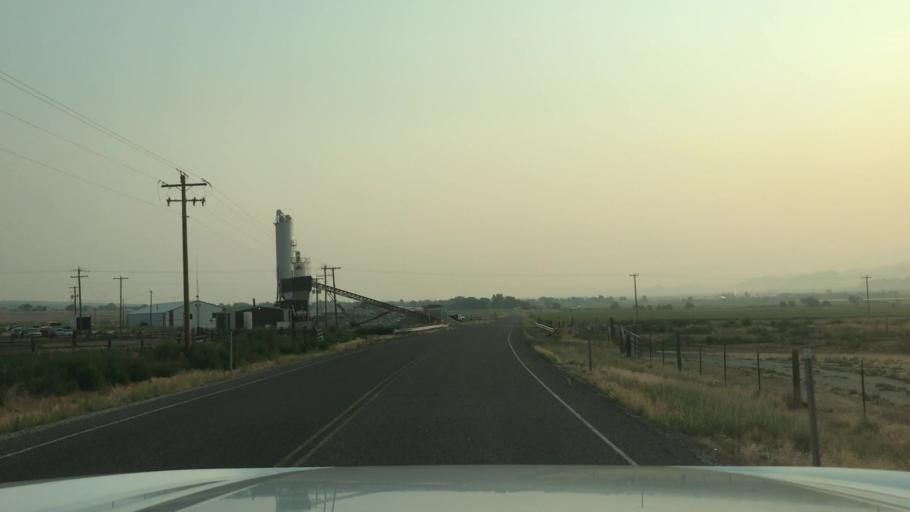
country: US
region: Utah
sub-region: Sevier County
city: Aurora
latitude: 38.9008
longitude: -111.9475
